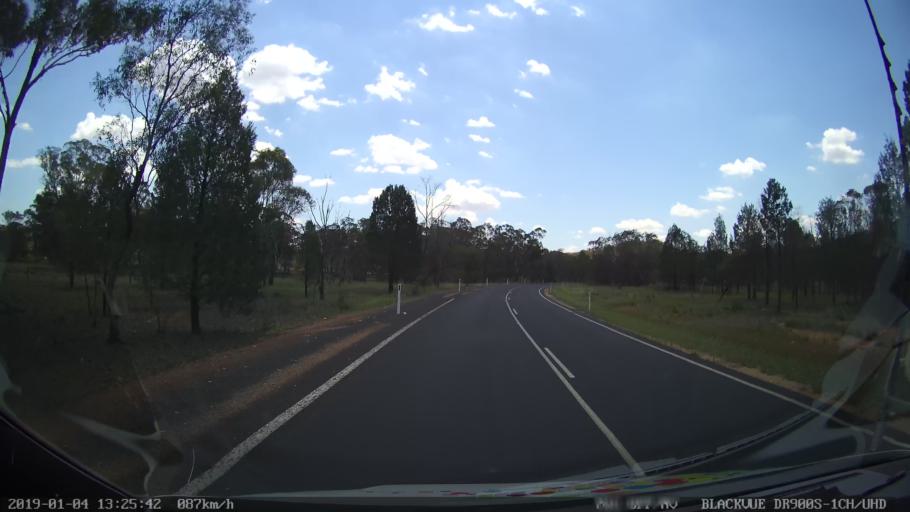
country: AU
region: New South Wales
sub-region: Parkes
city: Peak Hill
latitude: -32.6896
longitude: 148.5543
